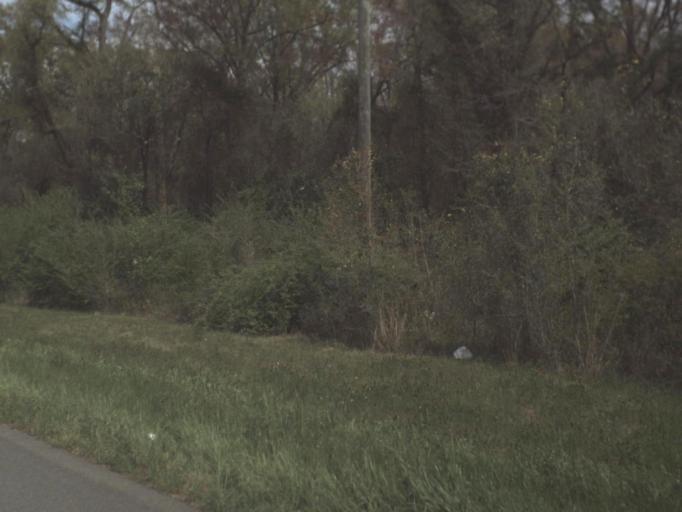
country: US
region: Florida
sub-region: Jackson County
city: Graceville
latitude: 30.9176
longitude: -85.4295
